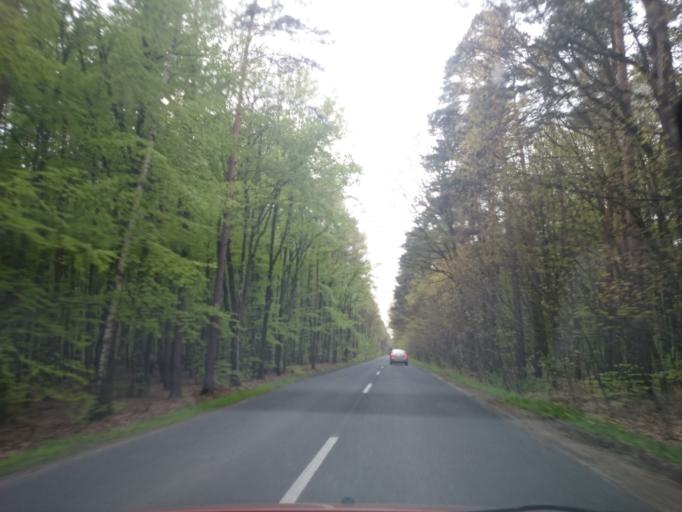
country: PL
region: Opole Voivodeship
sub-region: Powiat opolski
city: Niemodlin
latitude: 50.6239
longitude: 17.5627
